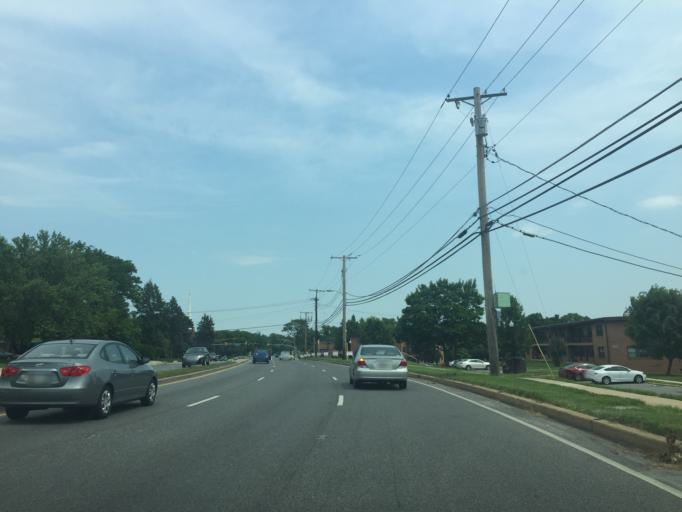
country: US
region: Maryland
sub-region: Baltimore County
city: Towson
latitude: 39.3755
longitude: -76.5794
